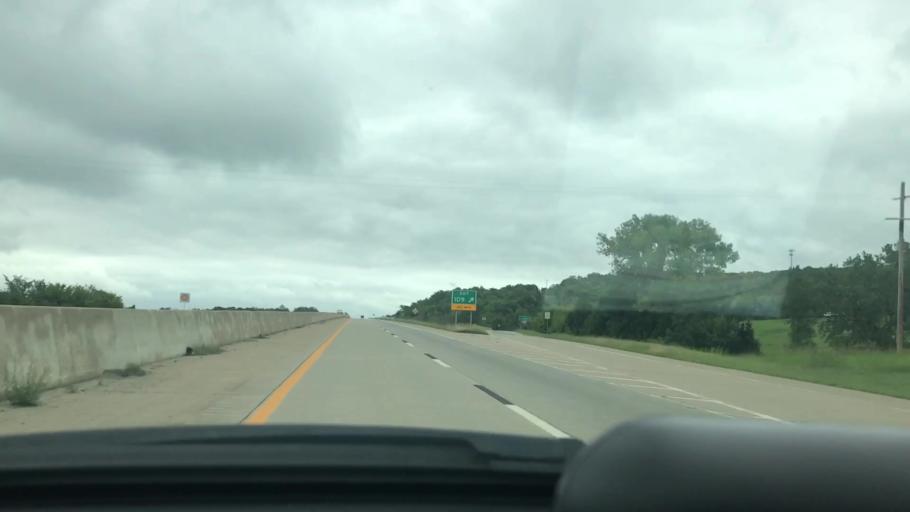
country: US
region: Oklahoma
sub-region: McIntosh County
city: Eufaula
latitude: 35.1691
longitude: -95.6507
